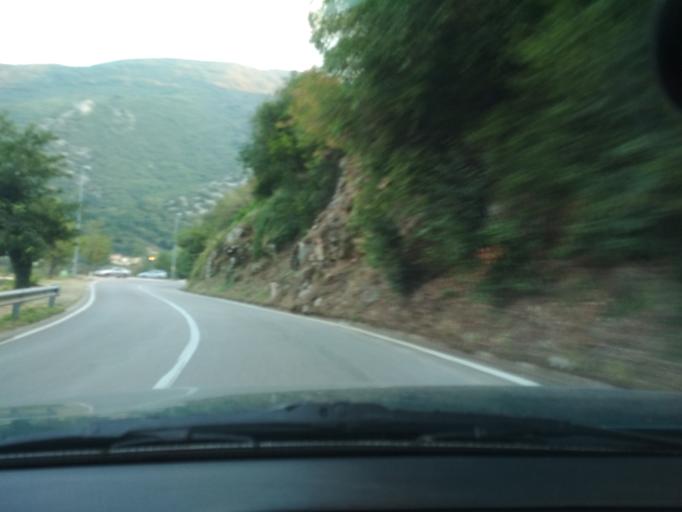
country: ME
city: Lipci
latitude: 42.4918
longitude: 18.6501
